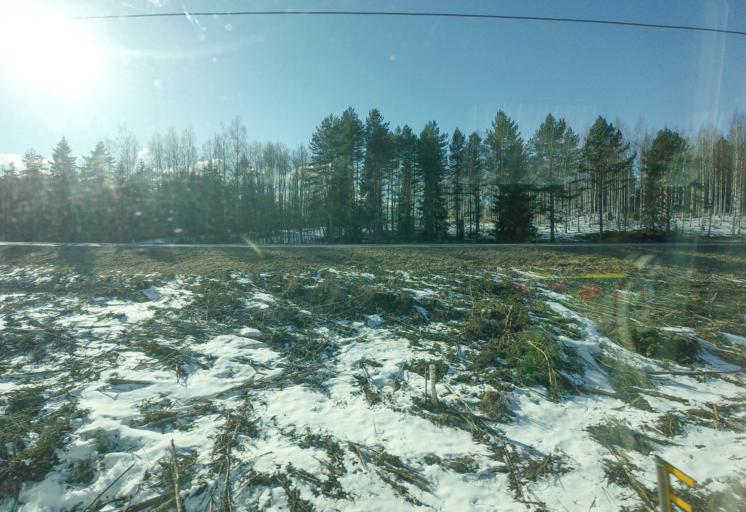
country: FI
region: South Karelia
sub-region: Imatra
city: Parikkala
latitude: 61.5171
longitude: 29.5125
